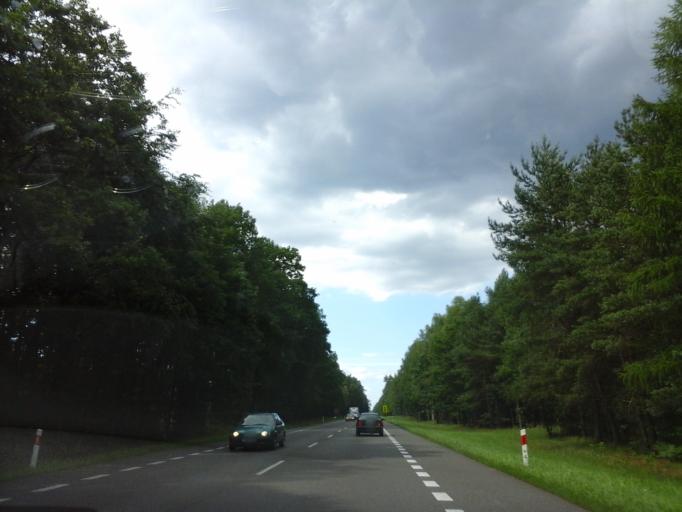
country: PL
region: West Pomeranian Voivodeship
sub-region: Powiat goleniowski
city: Przybiernow
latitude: 53.6911
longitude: 14.7947
